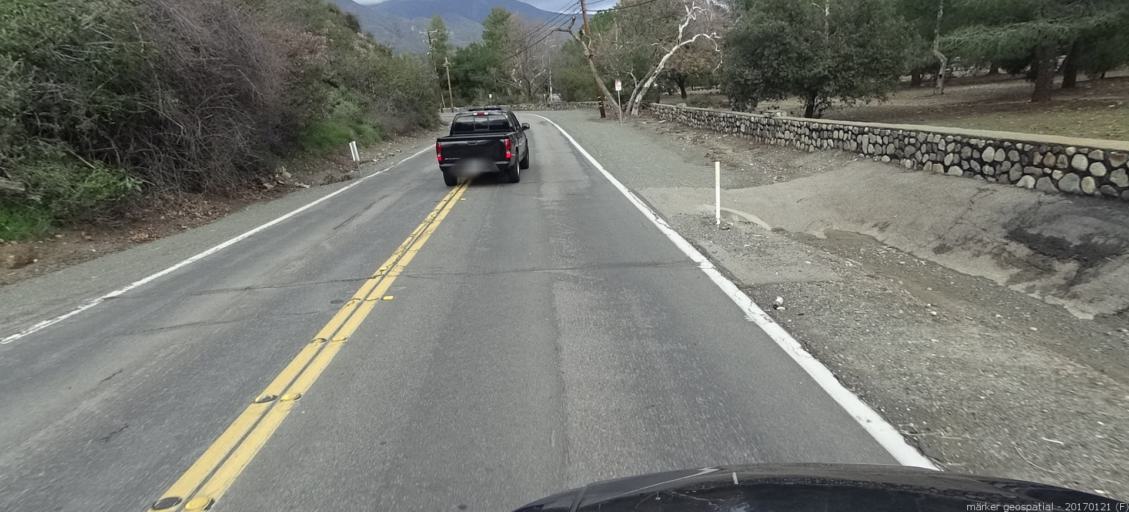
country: US
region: California
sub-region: Orange County
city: Trabuco Canyon
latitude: 33.6547
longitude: -117.5965
